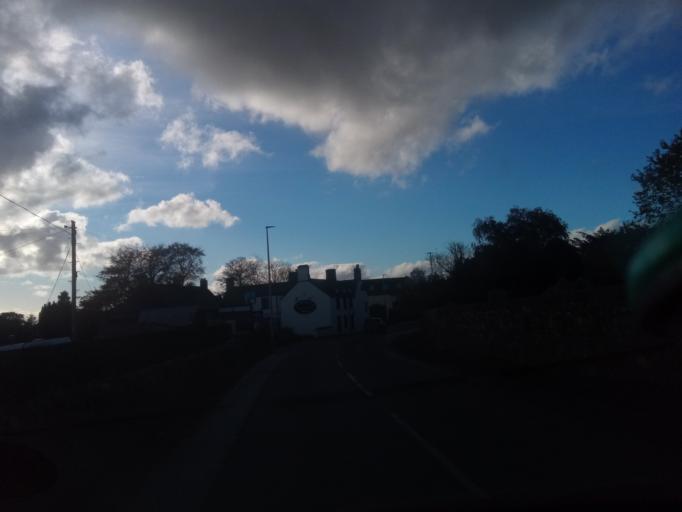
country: GB
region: Scotland
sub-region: The Scottish Borders
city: Chirnside
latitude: 55.7968
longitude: -2.2125
